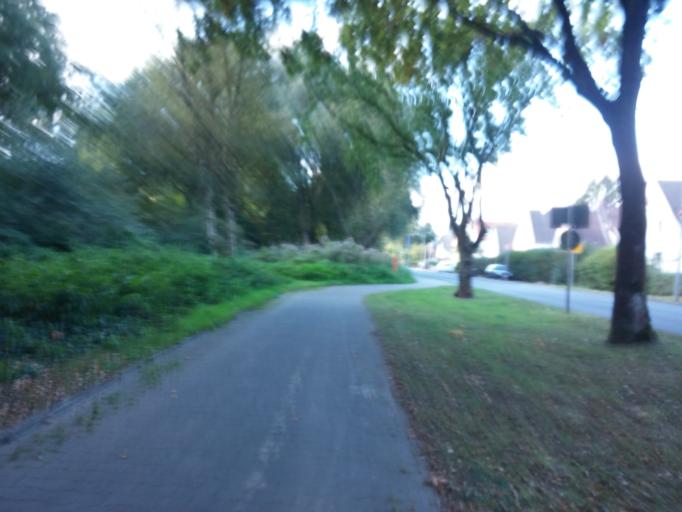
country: DE
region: North Rhine-Westphalia
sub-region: Regierungsbezirk Munster
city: Gladbeck
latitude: 51.6093
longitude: 6.9946
